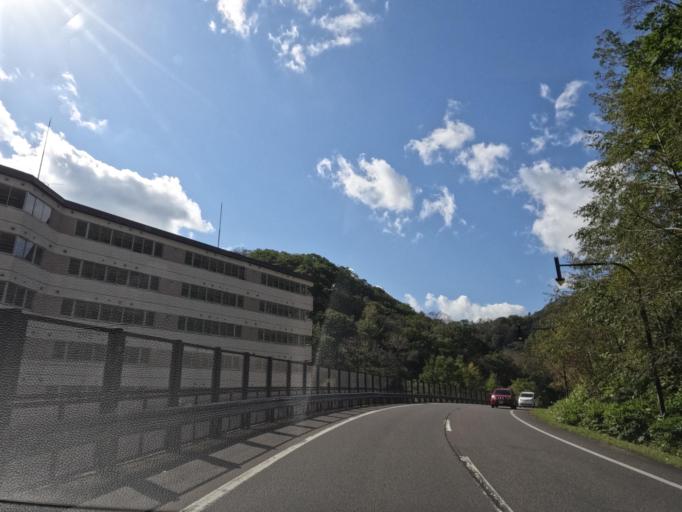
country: JP
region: Hokkaido
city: Shiraoi
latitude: 42.4869
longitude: 141.1477
